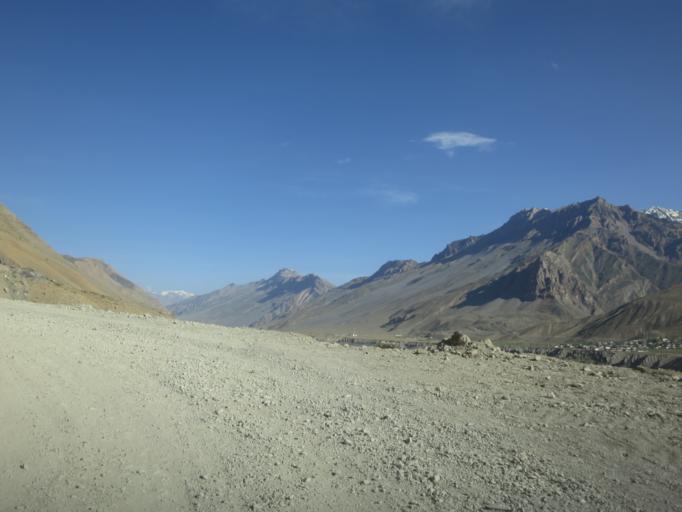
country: IN
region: Himachal Pradesh
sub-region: Shimla
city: Sarahan
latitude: 32.2768
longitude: 78.0253
